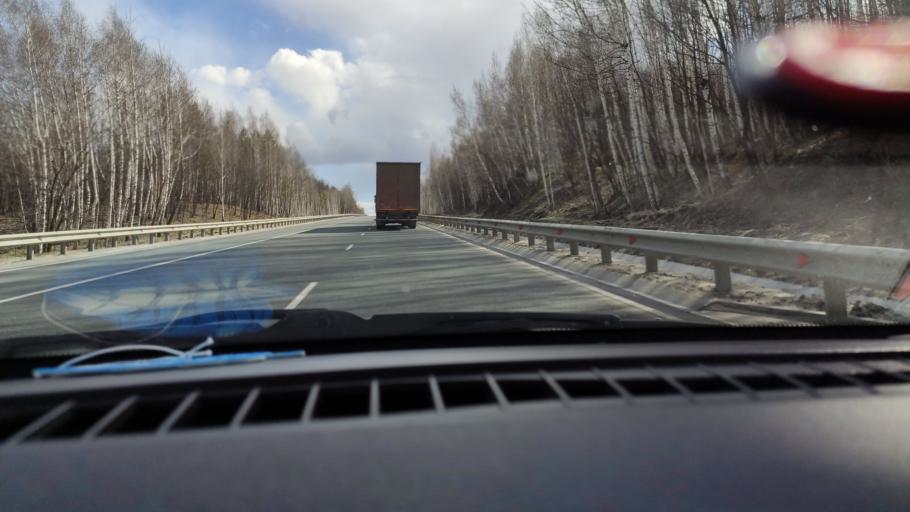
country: RU
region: Saratov
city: Khvalynsk
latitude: 52.4983
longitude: 48.0146
